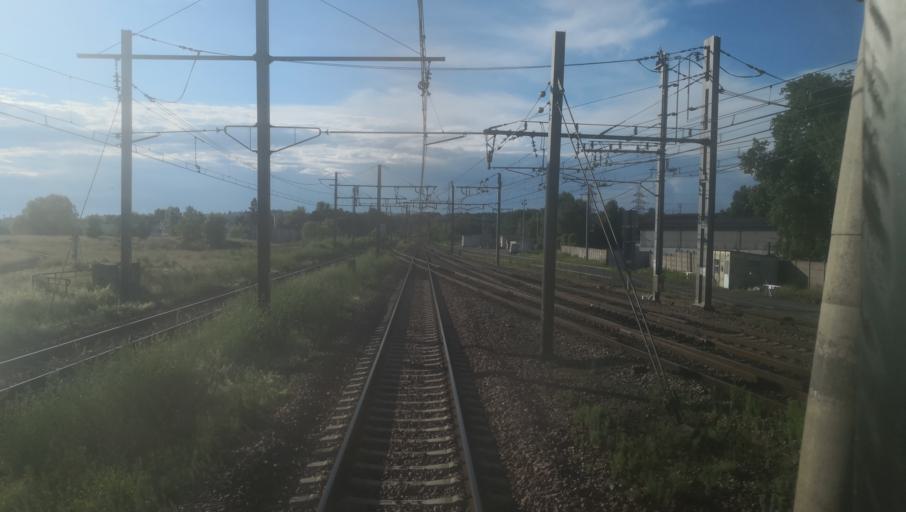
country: FR
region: Centre
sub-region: Departement du Cher
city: Vierzon
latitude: 47.2105
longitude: 2.0990
